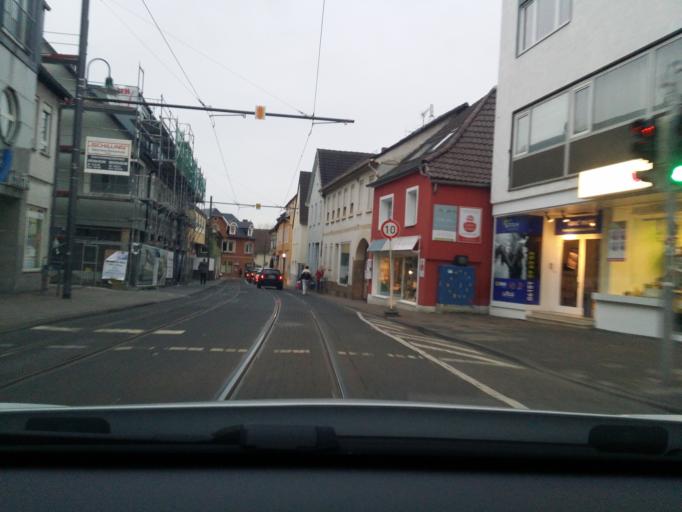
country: DE
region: Hesse
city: Pfungstadt
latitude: 49.8186
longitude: 8.6441
